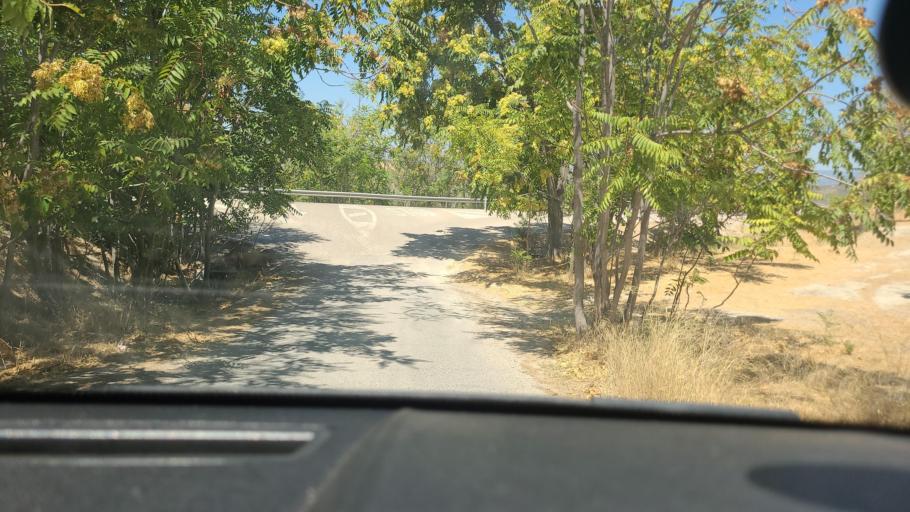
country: ES
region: Andalusia
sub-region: Provincia de Jaen
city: Jimena
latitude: 37.8357
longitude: -3.4616
